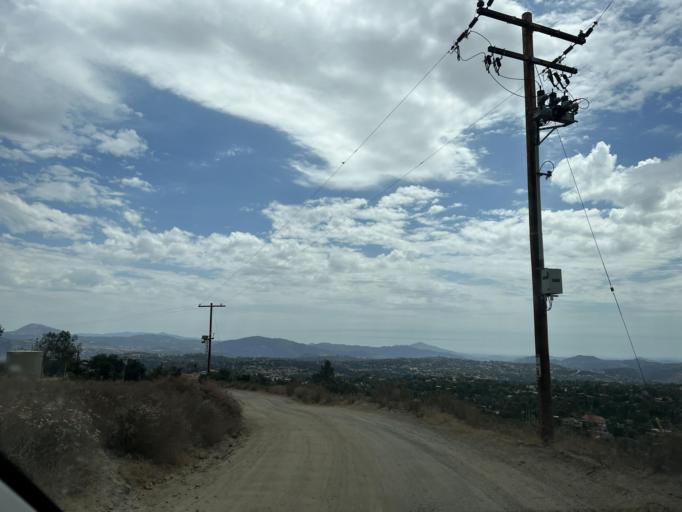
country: US
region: California
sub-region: San Diego County
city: Alpine
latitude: 32.8545
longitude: -116.7421
